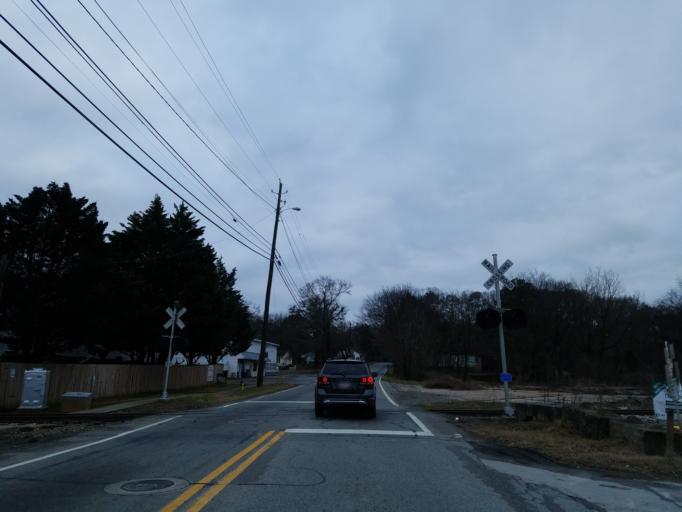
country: US
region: Georgia
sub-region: Bartow County
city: Cartersville
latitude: 34.1740
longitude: -84.8097
